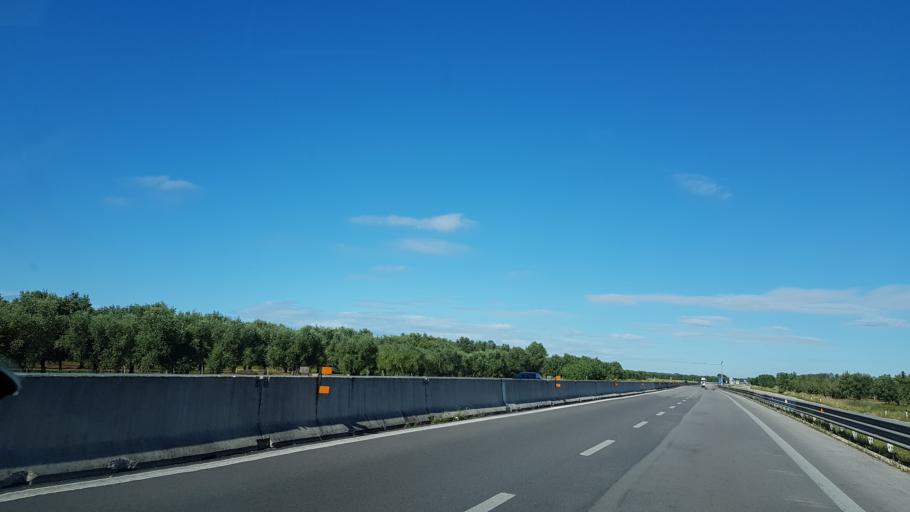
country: IT
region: Apulia
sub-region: Provincia di Brindisi
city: Latiano
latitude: 40.5648
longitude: 17.7597
